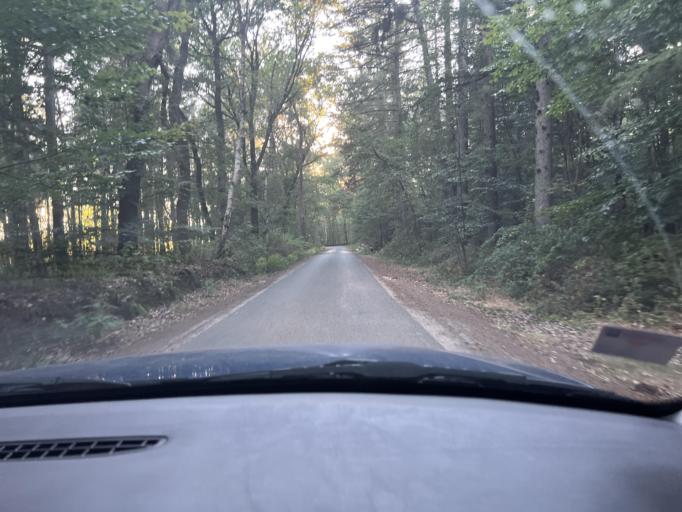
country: DE
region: Schleswig-Holstein
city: Weddingstedt
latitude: 54.2248
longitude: 9.1053
